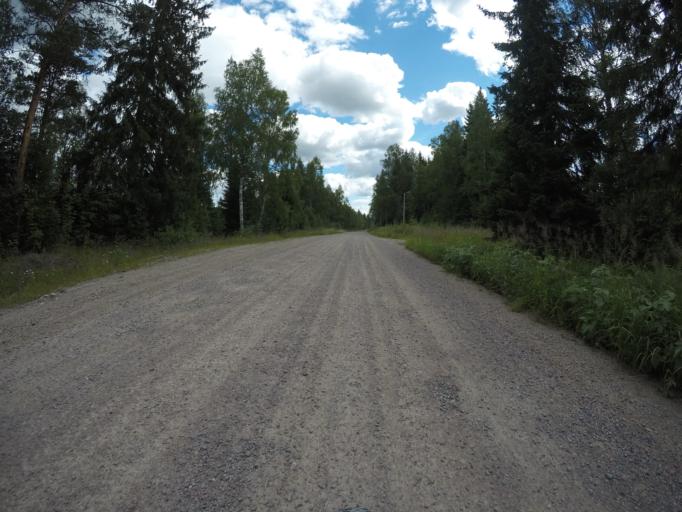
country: SE
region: Vaermland
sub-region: Filipstads Kommun
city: Lesjofors
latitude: 60.1323
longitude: 14.4134
